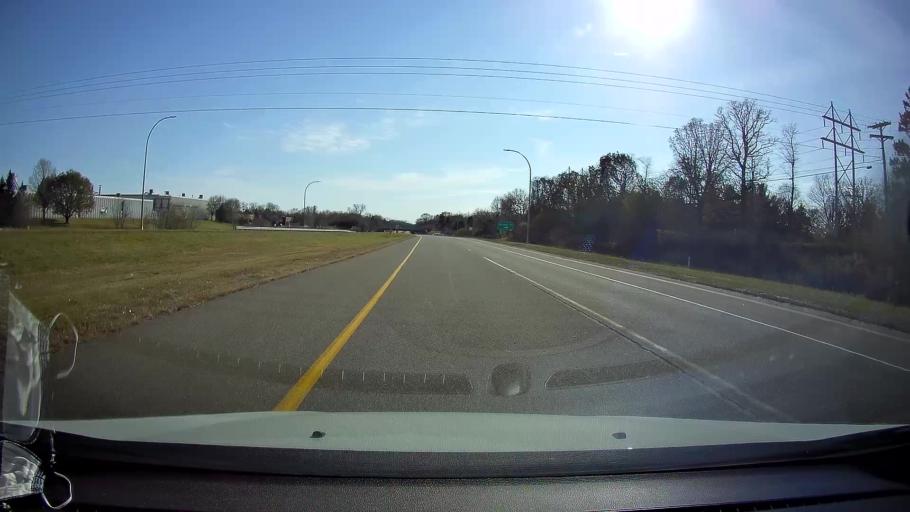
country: US
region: Minnesota
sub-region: Ramsey County
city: Arden Hills
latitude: 45.0578
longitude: -93.1572
